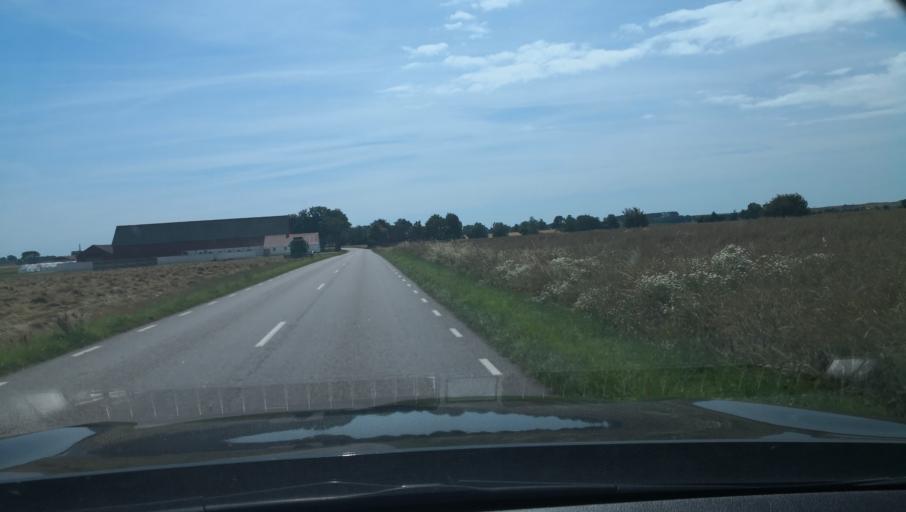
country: SE
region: Skane
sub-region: Ystads Kommun
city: Kopingebro
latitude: 55.4189
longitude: 14.1150
